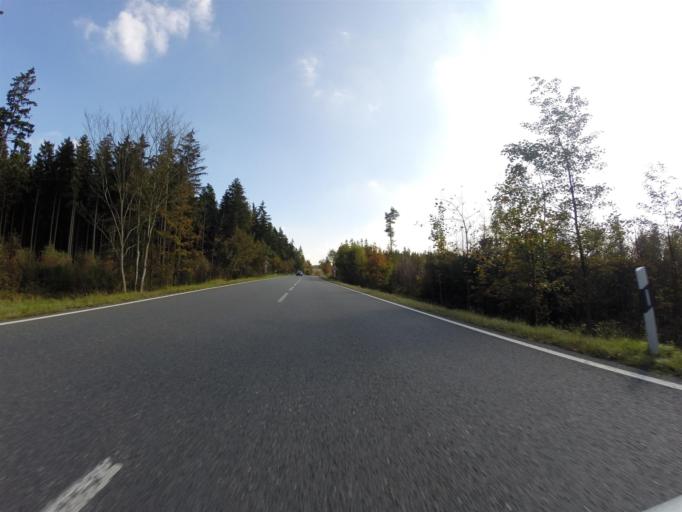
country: DE
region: Thuringia
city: Tanna
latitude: 50.4694
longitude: 11.8419
